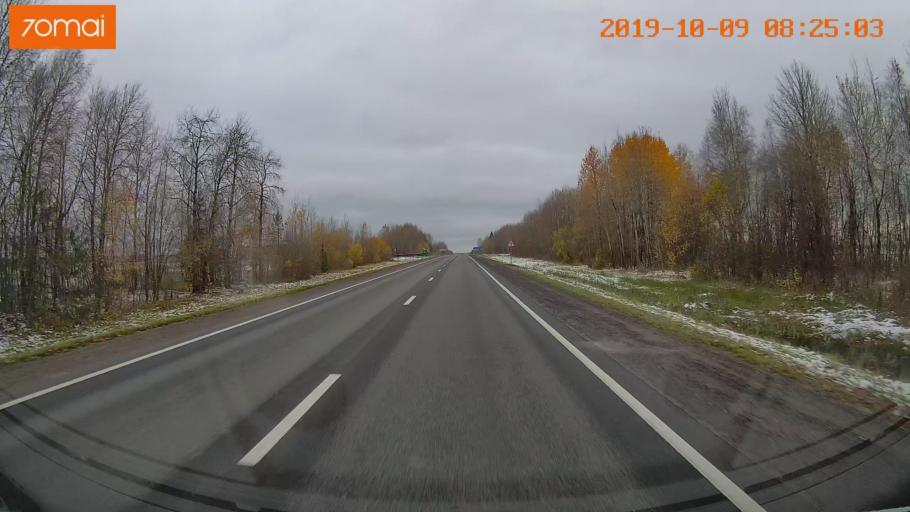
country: RU
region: Vologda
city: Gryazovets
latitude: 58.7753
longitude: 40.2747
